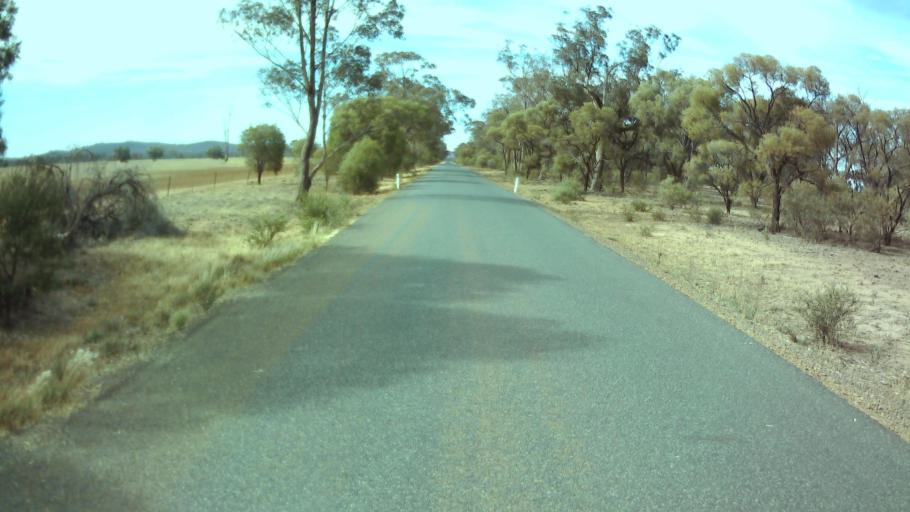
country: AU
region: New South Wales
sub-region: Weddin
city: Grenfell
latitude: -33.8701
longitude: 147.8582
